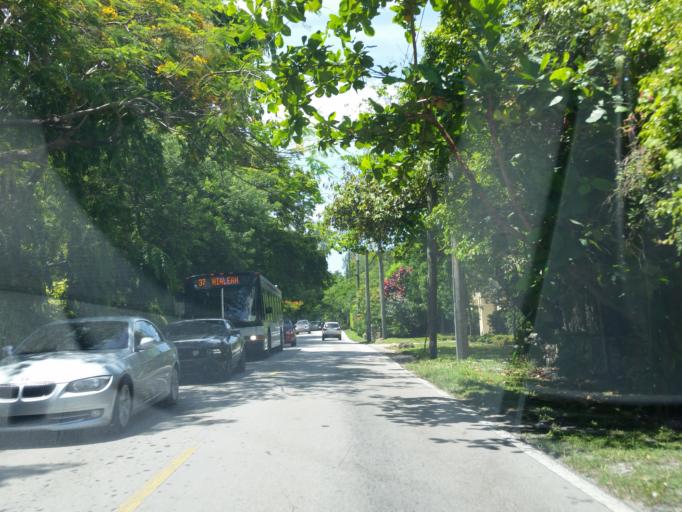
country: US
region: Florida
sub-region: Miami-Dade County
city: Coconut Grove
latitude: 25.7169
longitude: -80.2530
